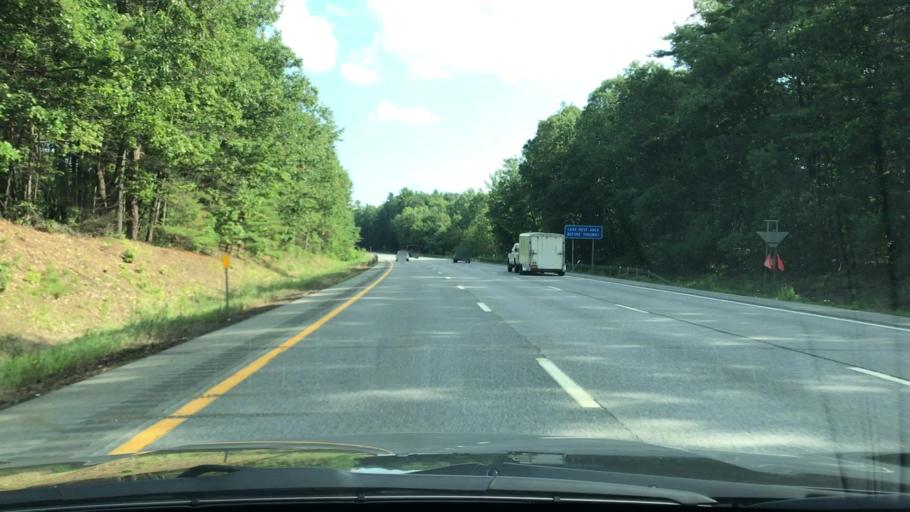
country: US
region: New York
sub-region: Warren County
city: West Glens Falls
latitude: 43.2854
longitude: -73.6812
